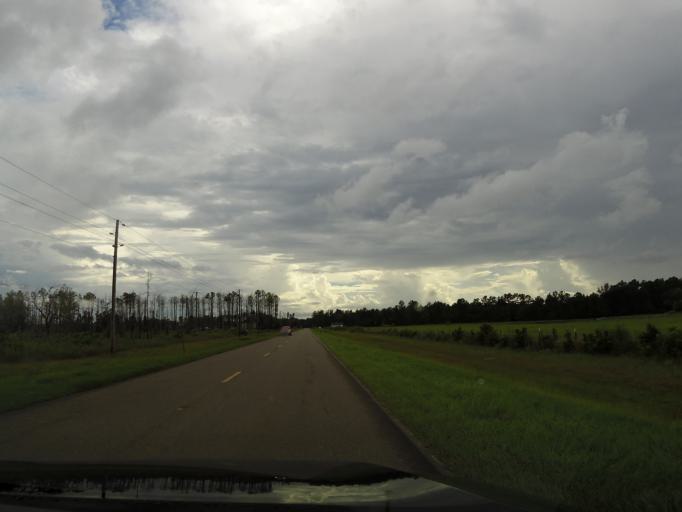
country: US
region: Florida
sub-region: Duval County
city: Baldwin
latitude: 30.4159
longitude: -82.0273
